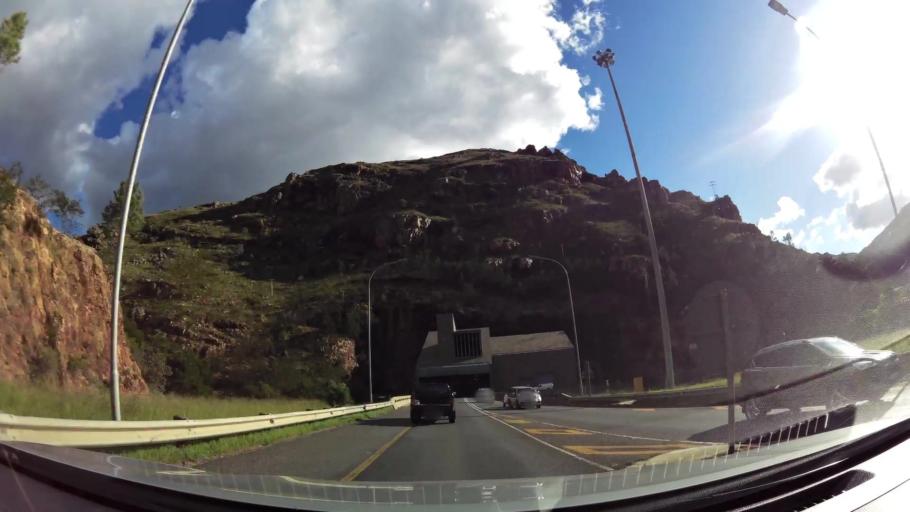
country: ZA
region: Western Cape
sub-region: Cape Winelands District Municipality
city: Paarl
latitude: -33.7329
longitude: 19.1146
